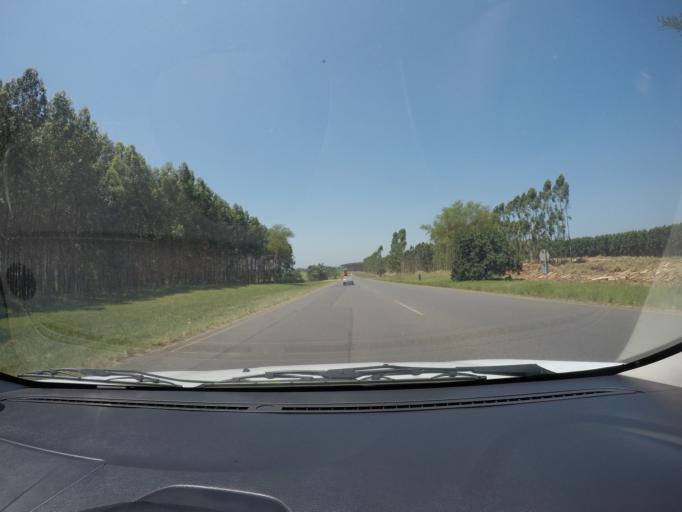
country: ZA
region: KwaZulu-Natal
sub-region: uThungulu District Municipality
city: eSikhawini
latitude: -28.8196
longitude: 31.9506
